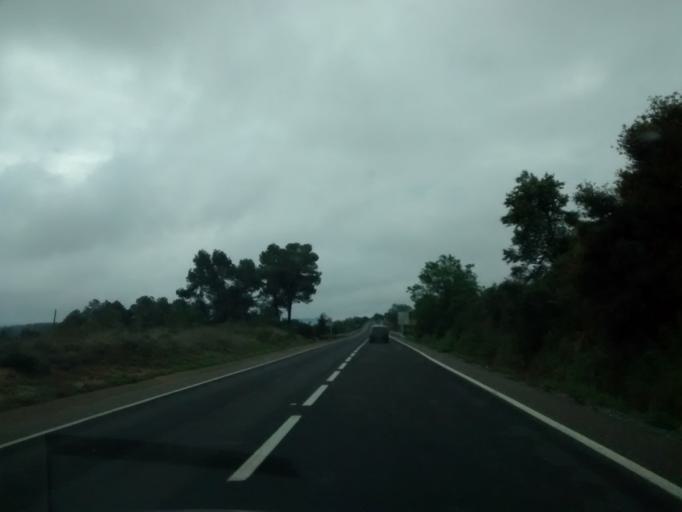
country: ES
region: Catalonia
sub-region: Provincia de Tarragona
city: Bot
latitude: 41.0539
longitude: 0.3622
